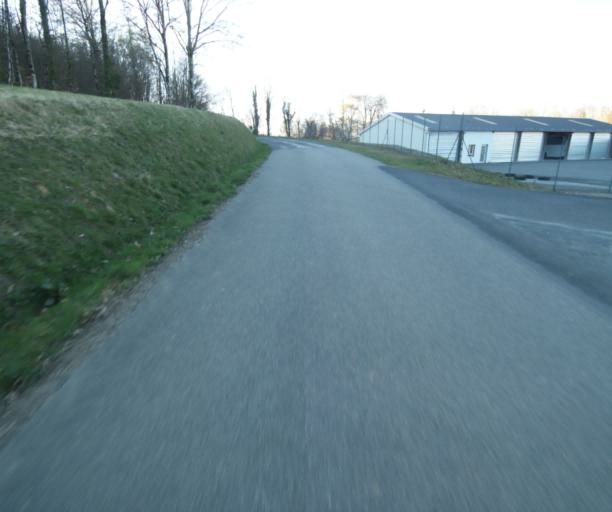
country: FR
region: Limousin
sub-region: Departement de la Correze
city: Seilhac
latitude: 45.3587
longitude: 1.7099
